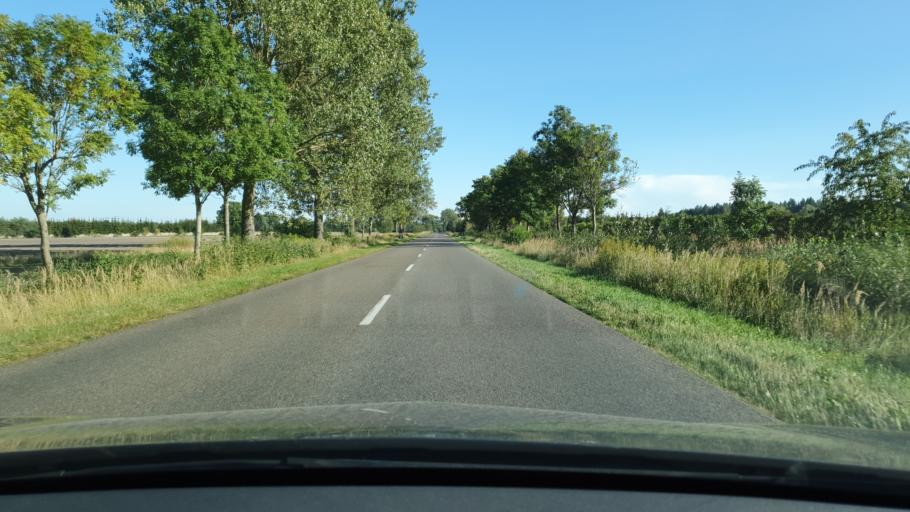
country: PL
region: West Pomeranian Voivodeship
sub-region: Powiat goleniowski
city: Przybiernow
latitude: 53.8364
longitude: 14.7617
